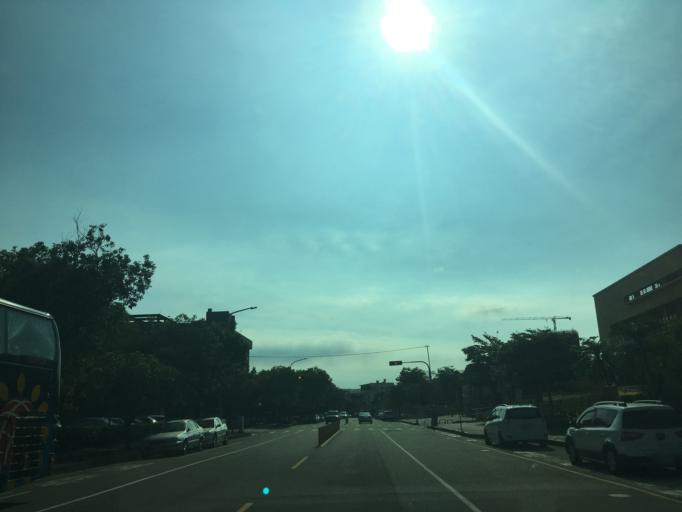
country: TW
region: Taiwan
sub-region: Taichung City
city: Taichung
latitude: 24.1557
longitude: 120.6334
